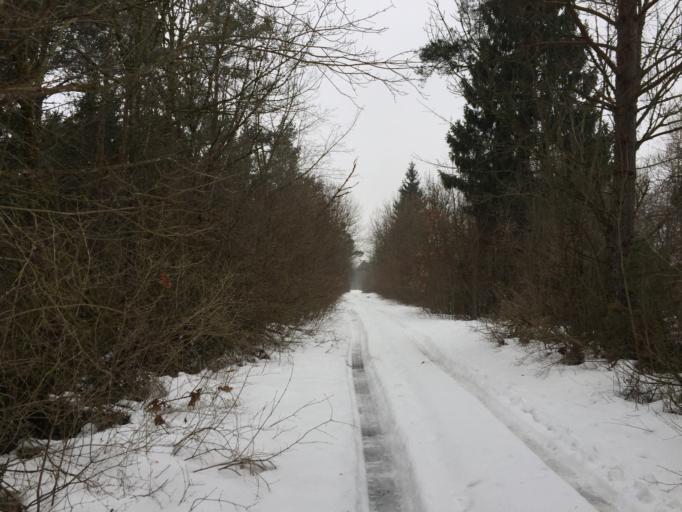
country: EE
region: Saare
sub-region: Orissaare vald
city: Orissaare
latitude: 58.4192
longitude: 22.8206
